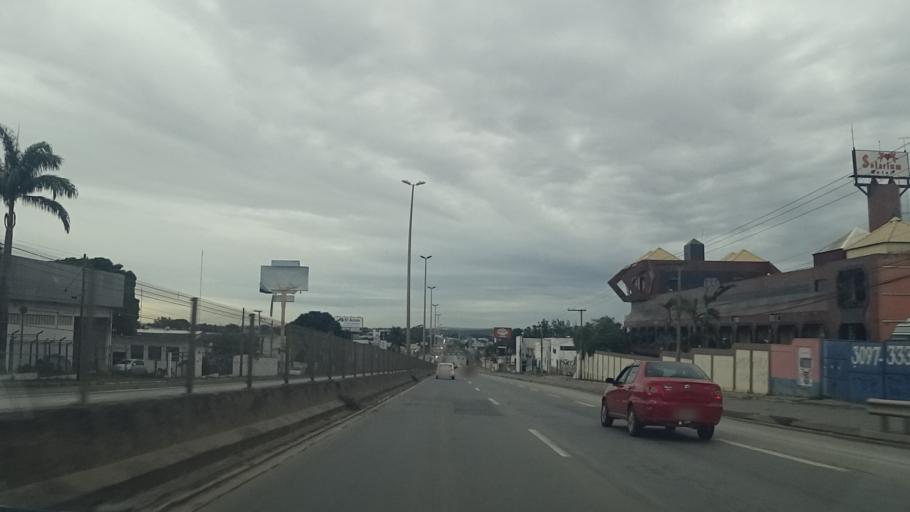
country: BR
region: Goias
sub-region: Goiania
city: Goiania
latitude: -16.7367
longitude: -49.2429
